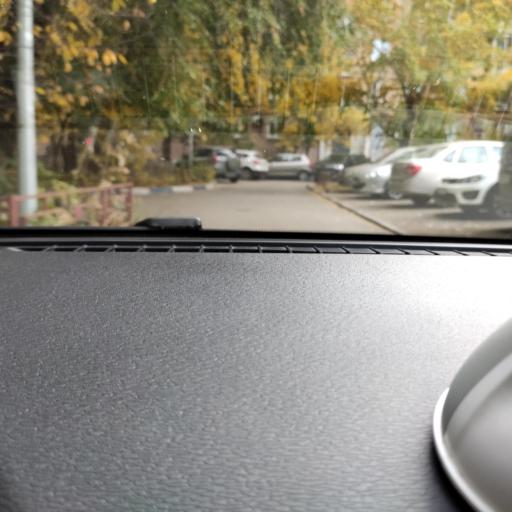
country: RU
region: Samara
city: Samara
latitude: 53.2078
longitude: 50.1326
